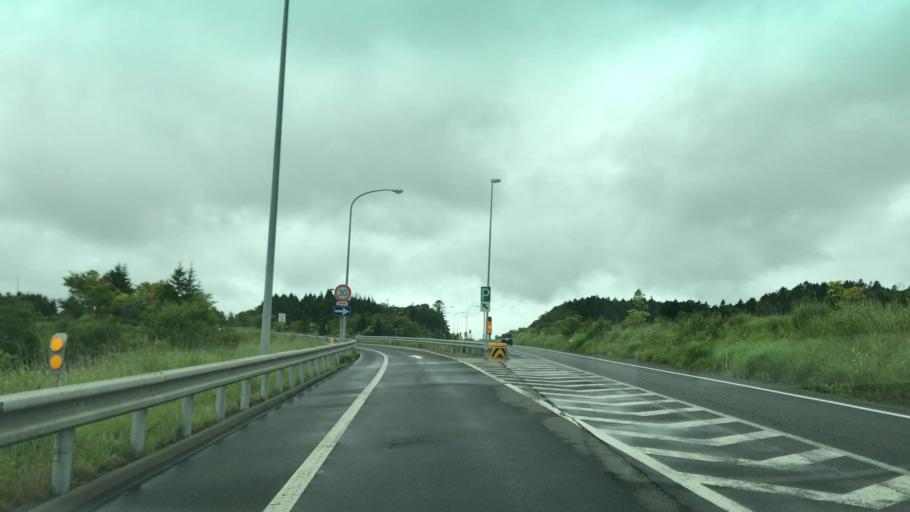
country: JP
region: Hokkaido
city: Muroran
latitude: 42.3845
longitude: 140.9905
